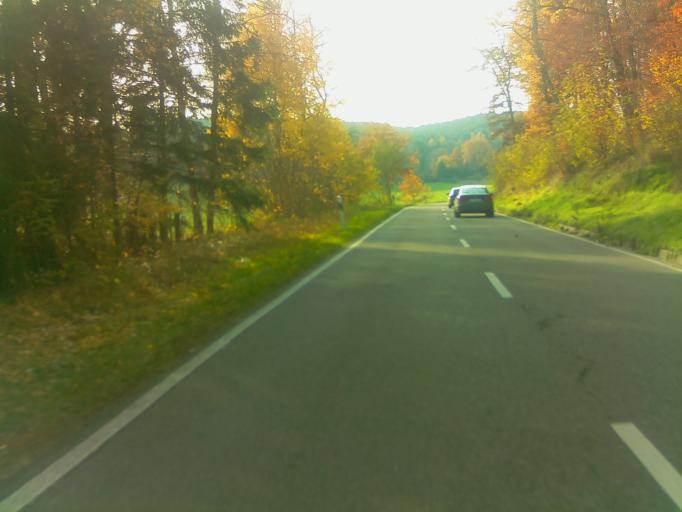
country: DE
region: Rheinland-Pfalz
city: Altleiningen
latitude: 49.5012
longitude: 8.0627
